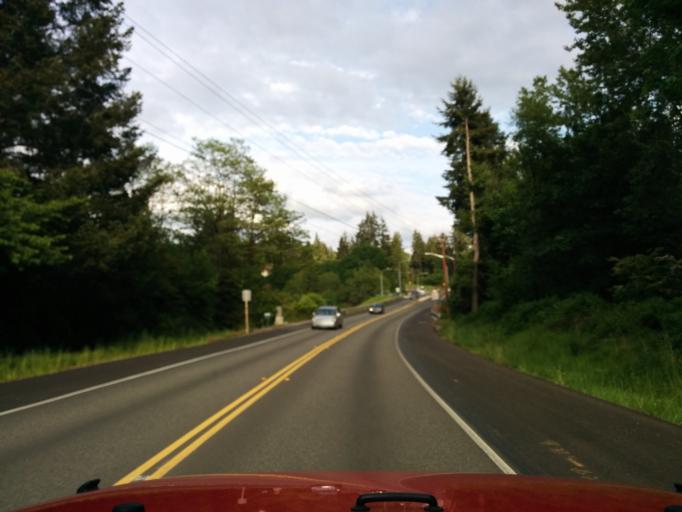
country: US
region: Washington
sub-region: King County
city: Redmond
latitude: 47.6887
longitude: -122.0830
